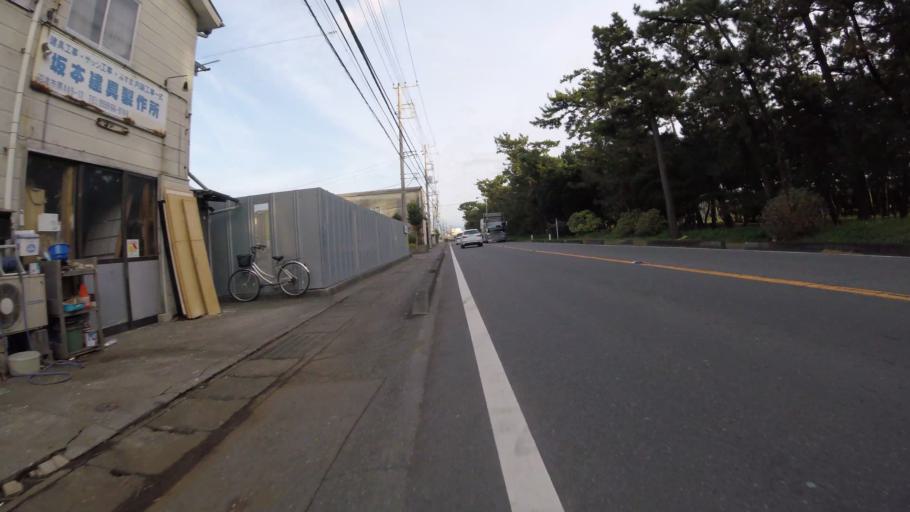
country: JP
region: Shizuoka
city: Numazu
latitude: 35.1246
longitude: 138.7903
